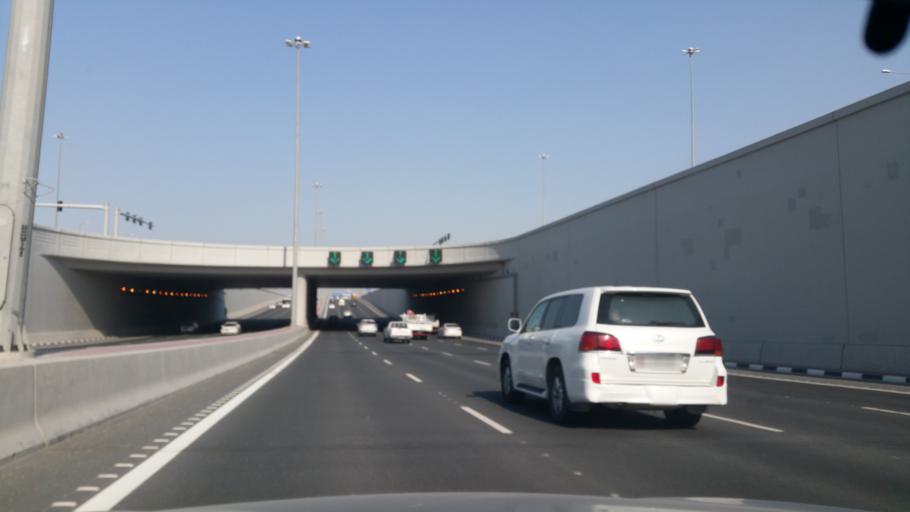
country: QA
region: Al Wakrah
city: Al Wukayr
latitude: 25.2006
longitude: 51.4747
